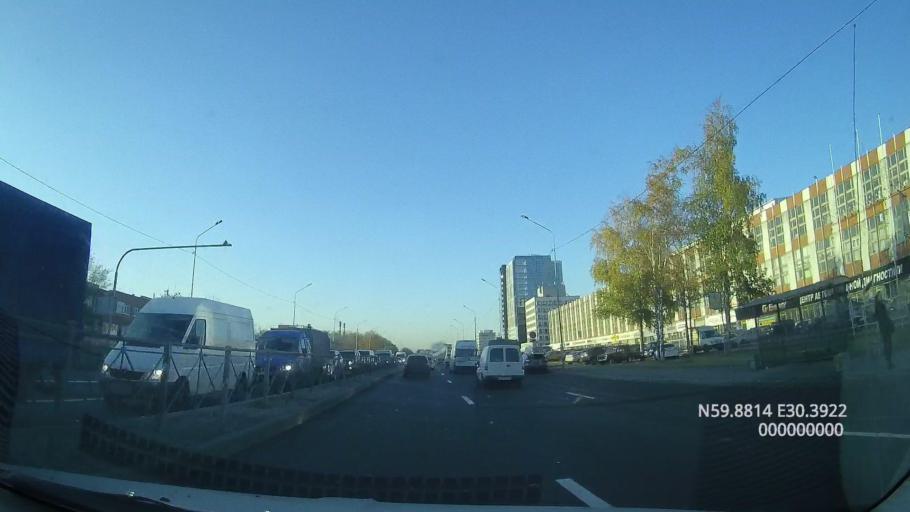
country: RU
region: St.-Petersburg
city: Kupchino
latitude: 59.8815
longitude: 30.3922
